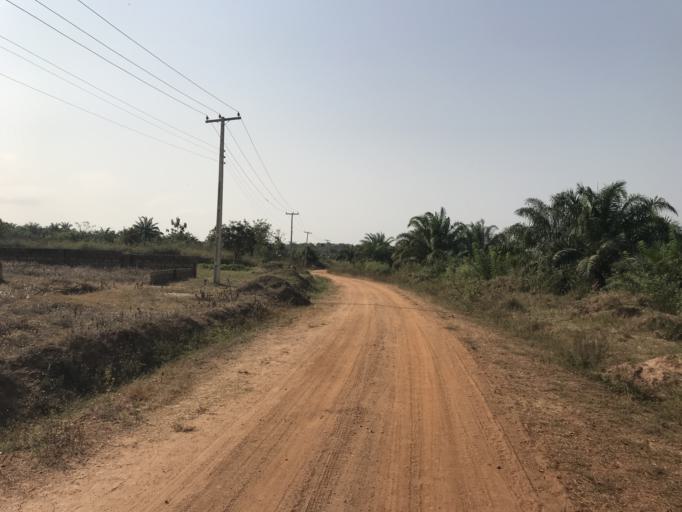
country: NG
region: Osun
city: Olupona
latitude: 7.6137
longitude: 4.1458
